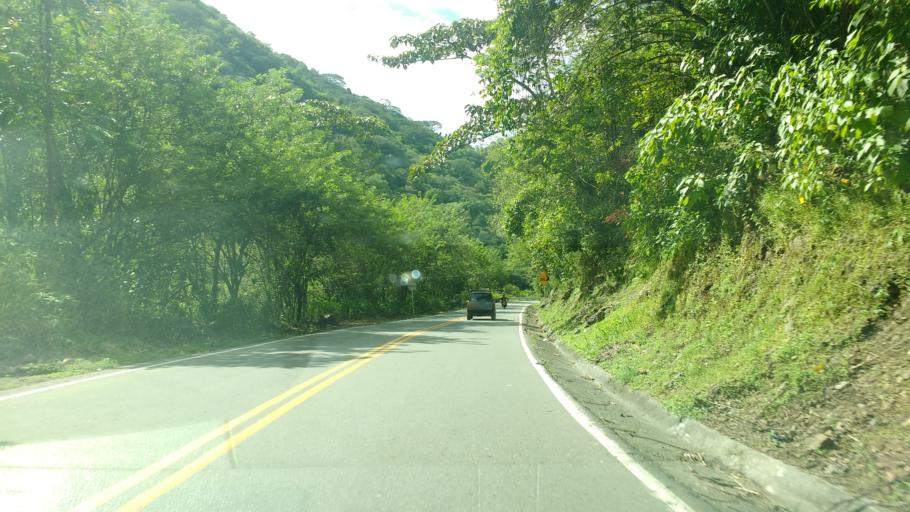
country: CO
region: Antioquia
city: Venecia
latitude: 5.9973
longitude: -75.7865
